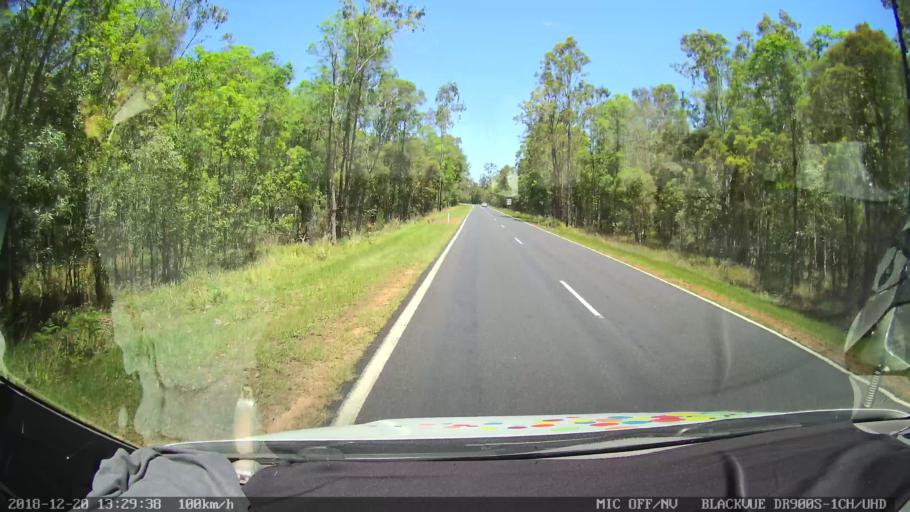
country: AU
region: New South Wales
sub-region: Clarence Valley
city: Gordon
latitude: -29.1918
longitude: 152.9905
